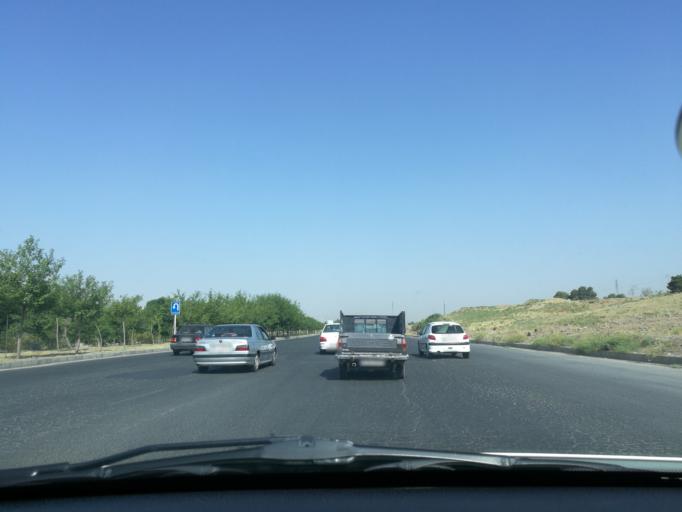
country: IR
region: Alborz
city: Karaj
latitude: 35.8632
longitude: 50.9336
